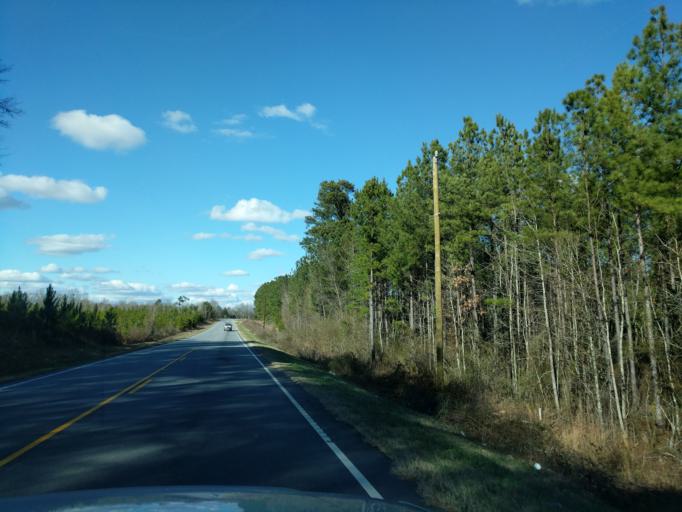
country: US
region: South Carolina
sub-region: Greenwood County
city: Ninety Six
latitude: 34.1018
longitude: -82.1030
